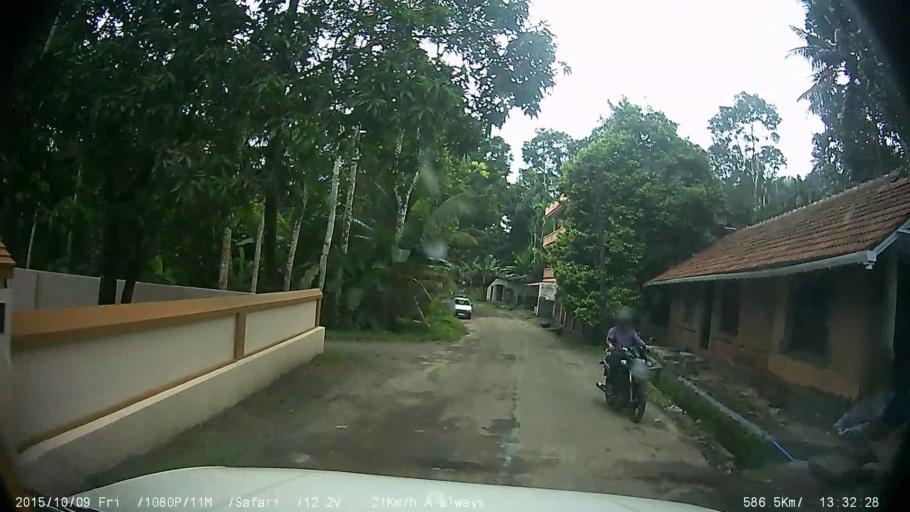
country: IN
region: Kerala
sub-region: Ernakulam
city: Ramamangalam
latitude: 9.9109
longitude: 76.5584
